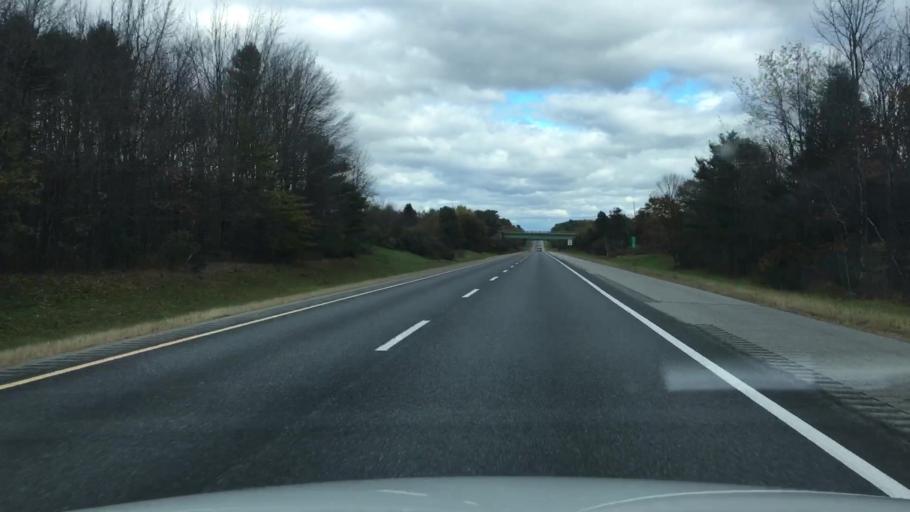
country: US
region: Maine
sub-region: Sagadahoc County
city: Topsham
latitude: 44.0280
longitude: -69.9134
